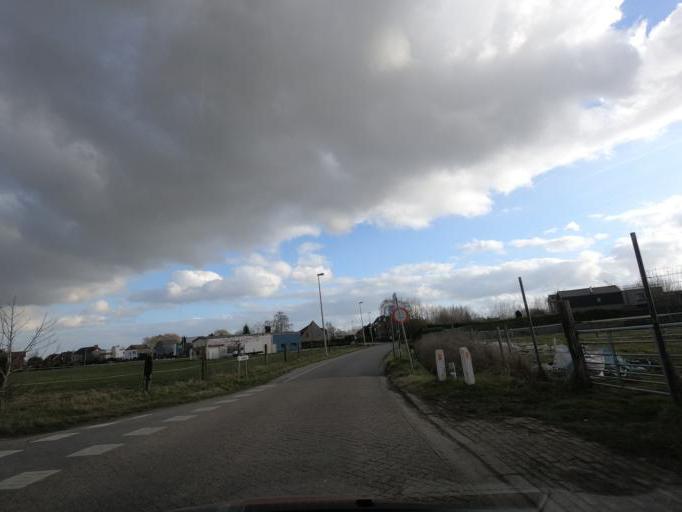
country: BE
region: Flanders
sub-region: Provincie Antwerpen
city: Borsbeek
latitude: 51.1855
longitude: 4.5067
